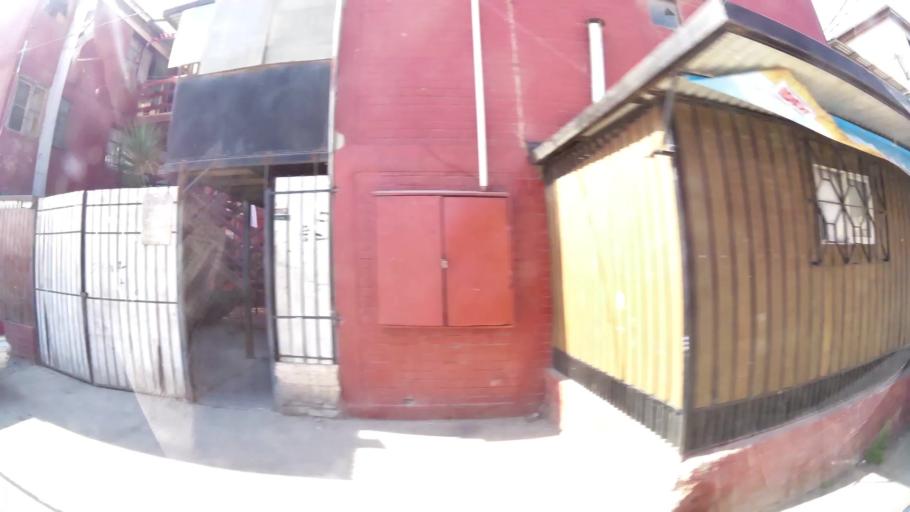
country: CL
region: Santiago Metropolitan
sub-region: Provincia de Maipo
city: San Bernardo
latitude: -33.5225
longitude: -70.7021
